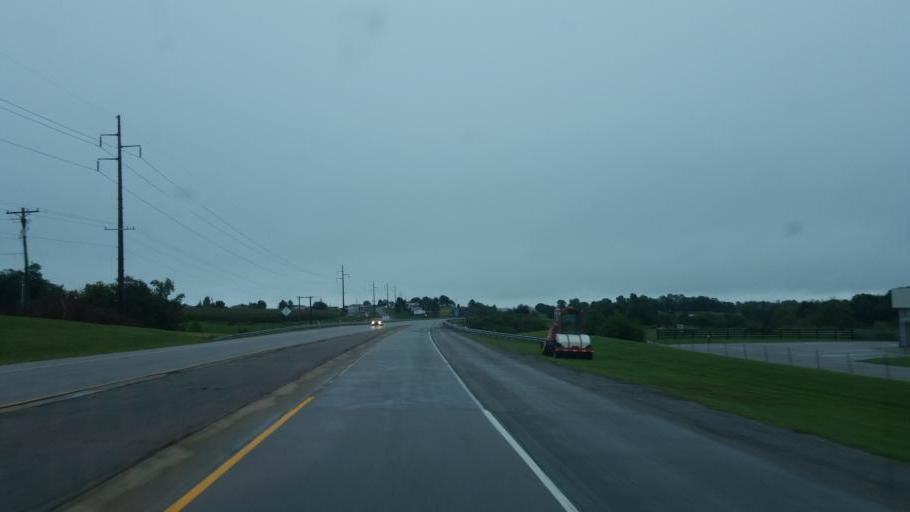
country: US
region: Kentucky
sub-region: Fleming County
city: Flemingsburg
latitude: 38.4116
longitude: -83.7370
